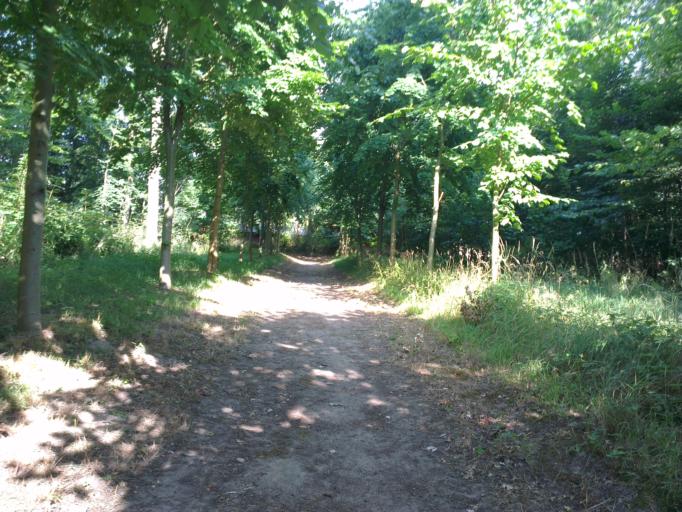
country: DK
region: Capital Region
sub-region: Frederikssund Kommune
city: Jaegerspris
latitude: 55.8568
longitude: 11.9848
